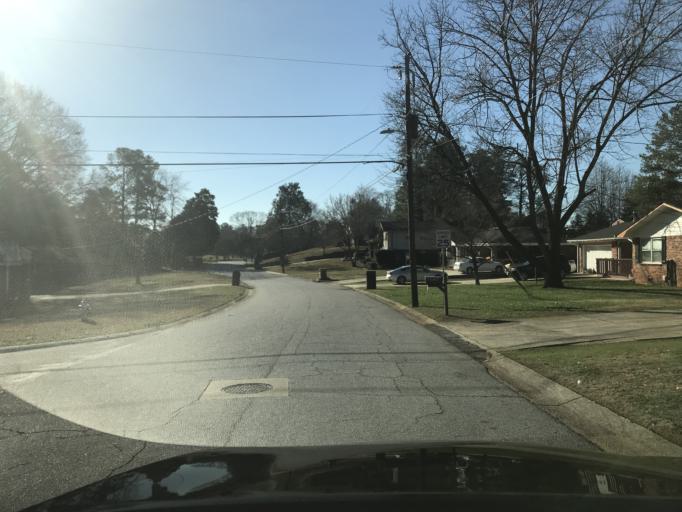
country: US
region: Georgia
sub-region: Clayton County
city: Morrow
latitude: 33.5667
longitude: -84.3686
